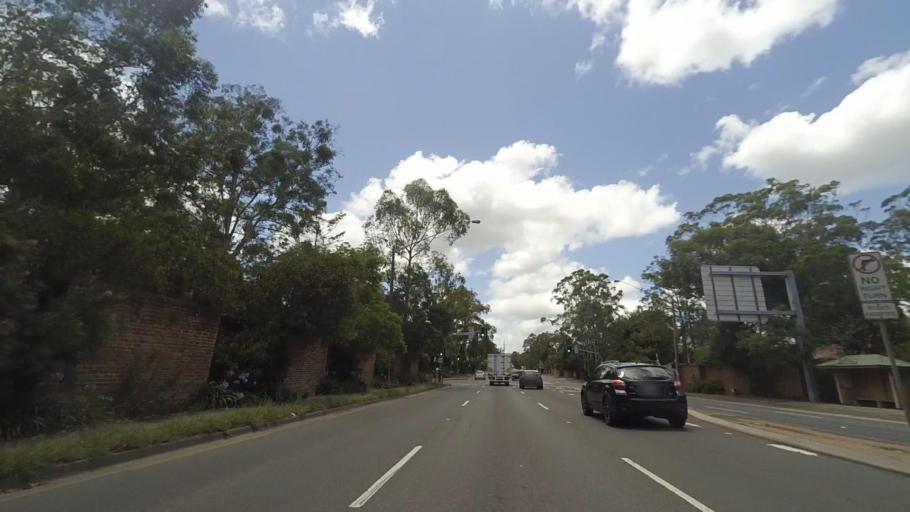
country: AU
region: New South Wales
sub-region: The Hills Shire
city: West Pennant
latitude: -33.7463
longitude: 151.0516
